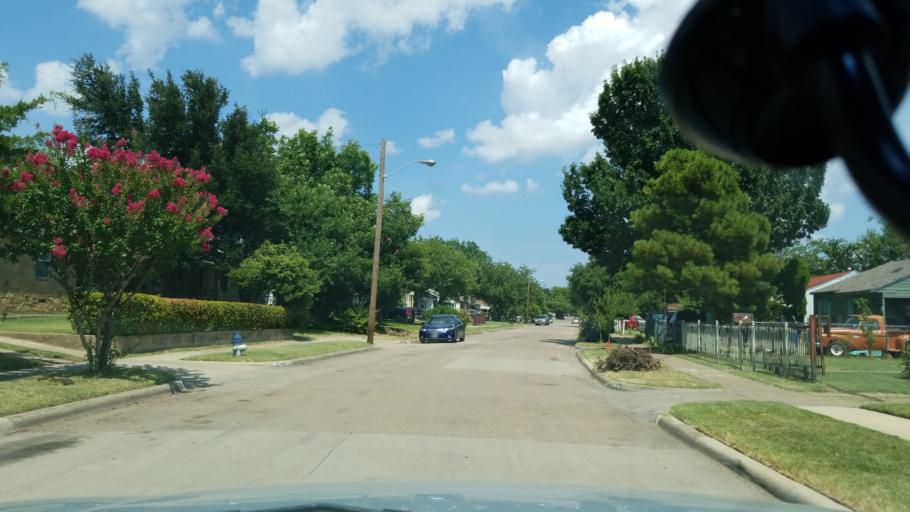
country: US
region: Texas
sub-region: Dallas County
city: Cockrell Hill
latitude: 32.7239
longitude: -96.8800
